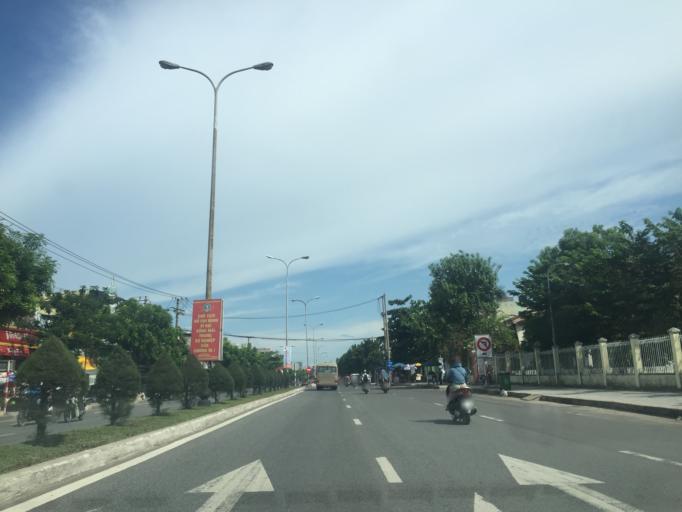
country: VN
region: Da Nang
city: Lien Chieu
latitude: 16.0621
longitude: 108.1600
